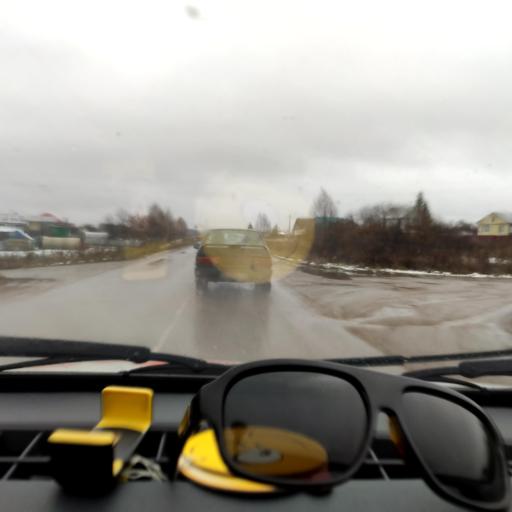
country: RU
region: Bashkortostan
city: Iglino
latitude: 54.8769
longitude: 56.5604
